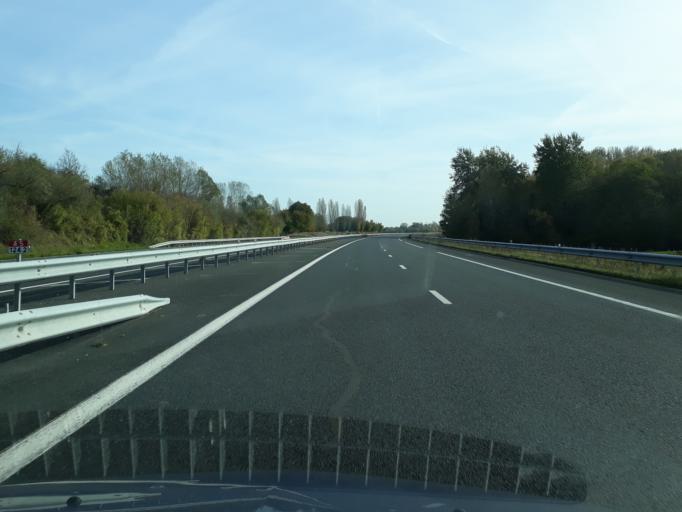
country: FR
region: Champagne-Ardenne
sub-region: Departement de l'Aube
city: Saint-Pouange
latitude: 48.2332
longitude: 4.0474
